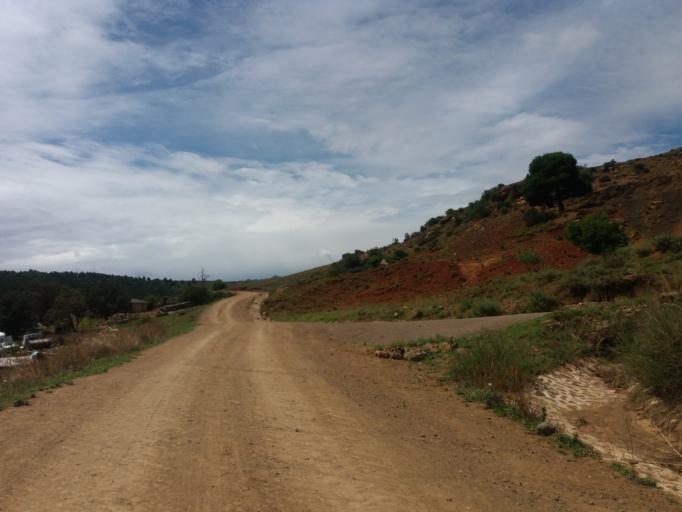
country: LS
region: Quthing
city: Quthing
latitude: -30.4119
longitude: 27.6950
